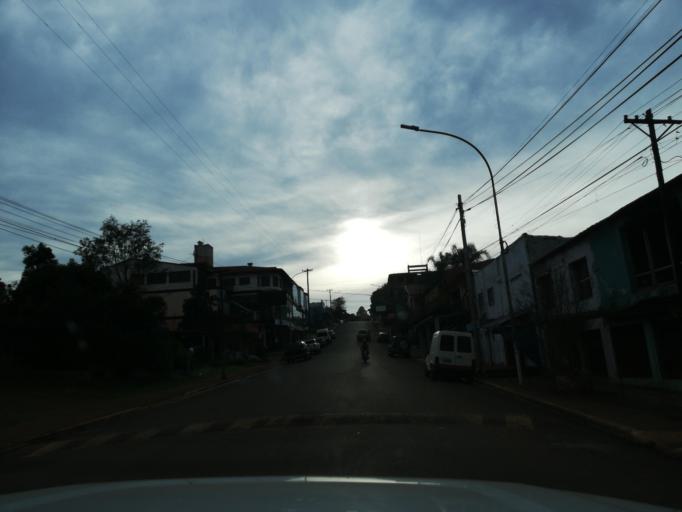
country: AR
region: Misiones
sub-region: Departamento de San Pedro
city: San Pedro
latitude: -26.6219
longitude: -54.1089
